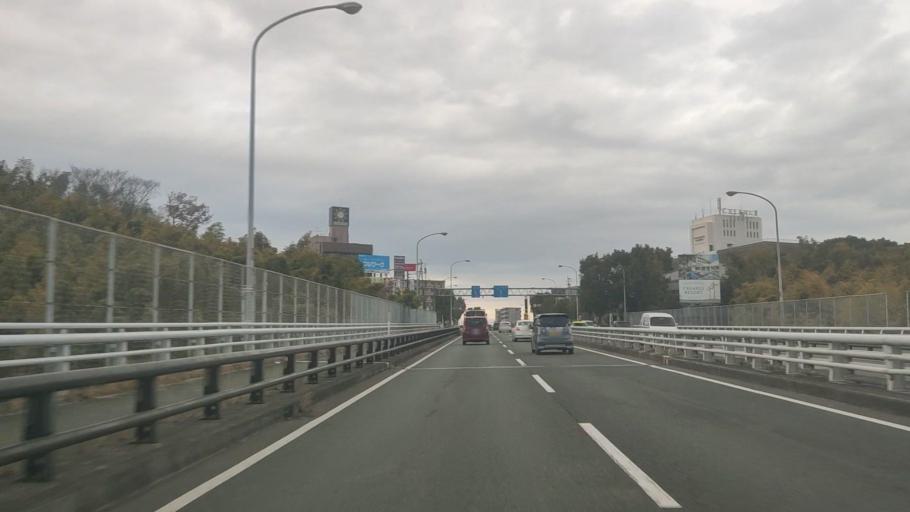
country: JP
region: Kumamoto
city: Ozu
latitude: 32.8495
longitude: 130.7825
